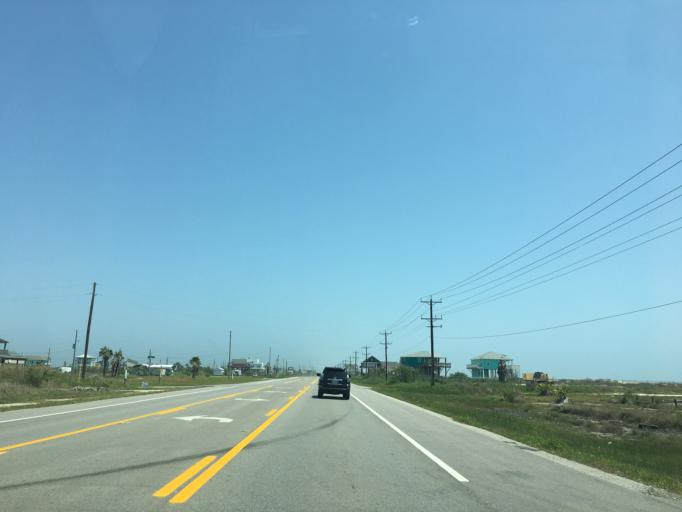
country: US
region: Texas
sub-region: Galveston County
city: Bolivar Peninsula
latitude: 29.5097
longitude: -94.4967
